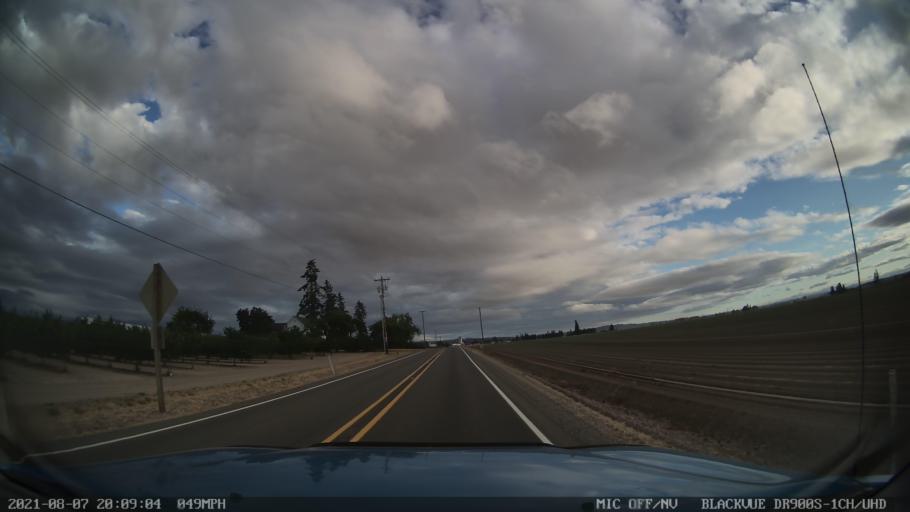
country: US
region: Oregon
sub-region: Marion County
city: Silverton
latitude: 44.9755
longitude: -122.8774
